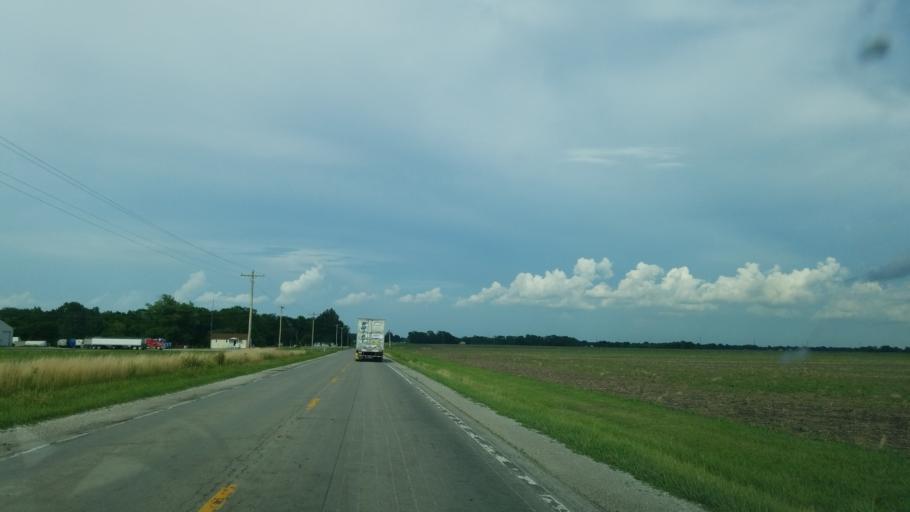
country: US
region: Illinois
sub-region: Marion County
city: Sandoval
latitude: 38.6165
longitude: -89.1531
